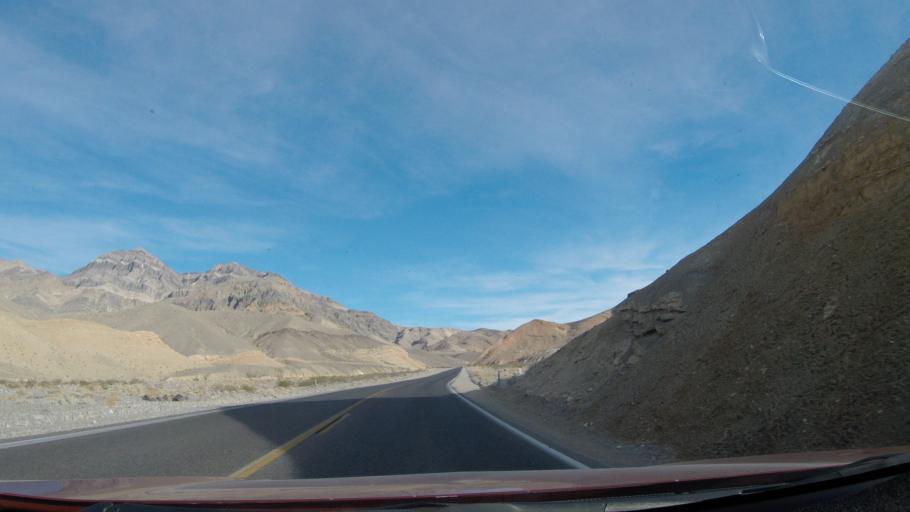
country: US
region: Nevada
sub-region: Nye County
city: Beatty
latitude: 36.3743
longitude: -116.6750
